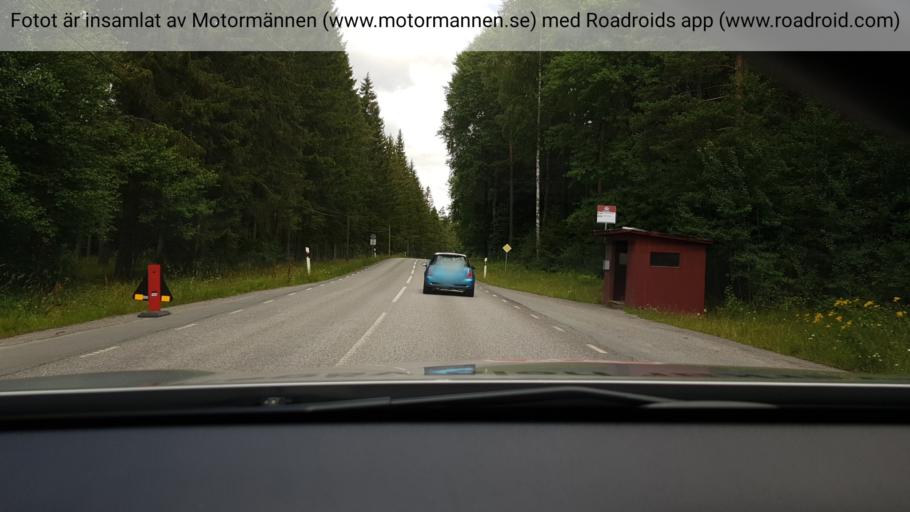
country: SE
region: Stockholm
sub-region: Haninge Kommun
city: Haninge
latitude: 59.1408
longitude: 18.1854
